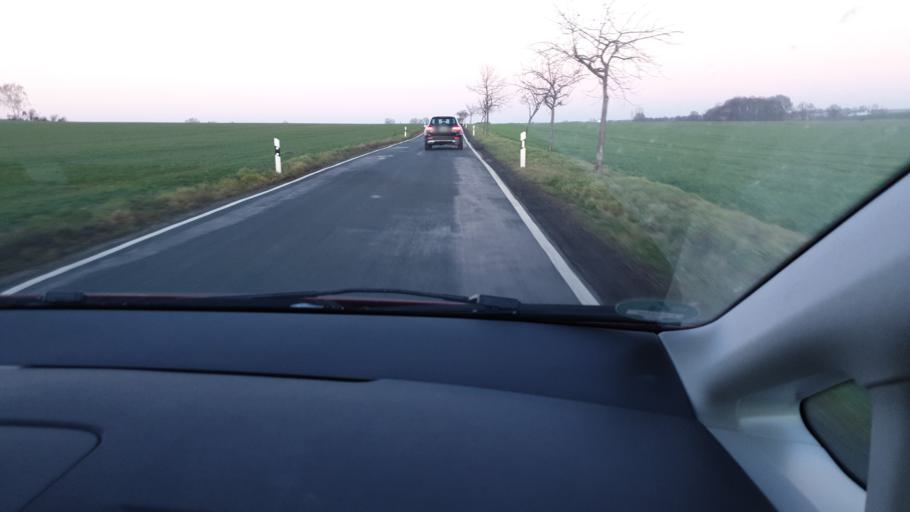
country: DE
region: Saxony
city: Mockrehna
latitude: 51.4624
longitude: 12.7875
